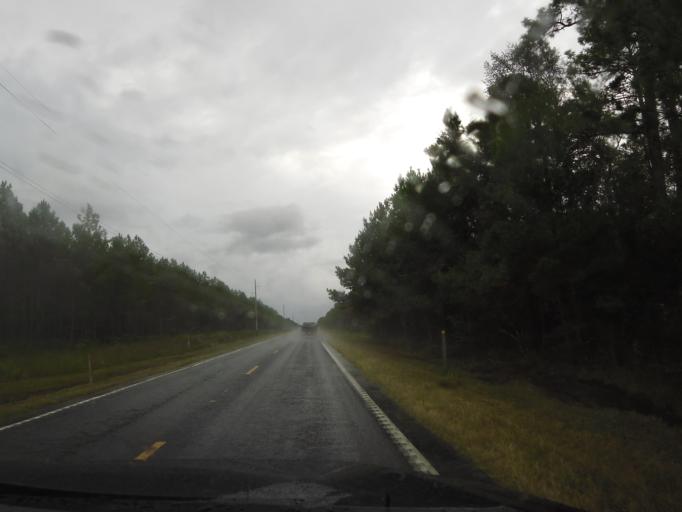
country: US
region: Florida
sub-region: Baker County
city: Macclenny
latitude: 30.4117
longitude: -82.1072
